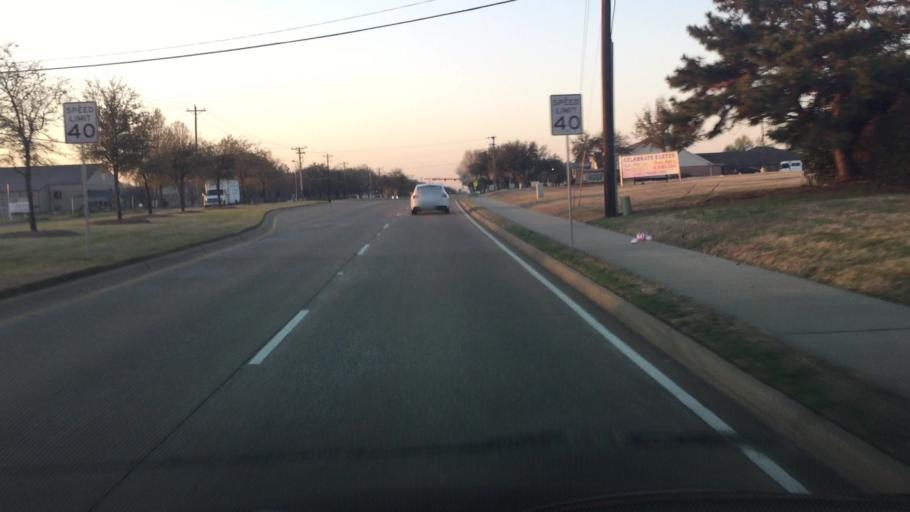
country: US
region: Texas
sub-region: Denton County
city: Highland Village
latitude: 33.0694
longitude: -97.0620
